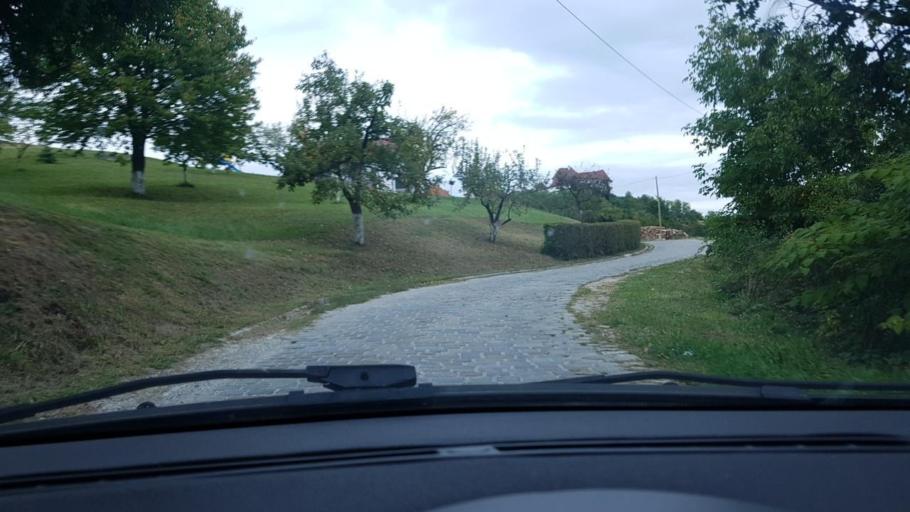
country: SI
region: Podcetrtek
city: Podcetrtek
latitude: 46.1517
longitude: 15.6462
